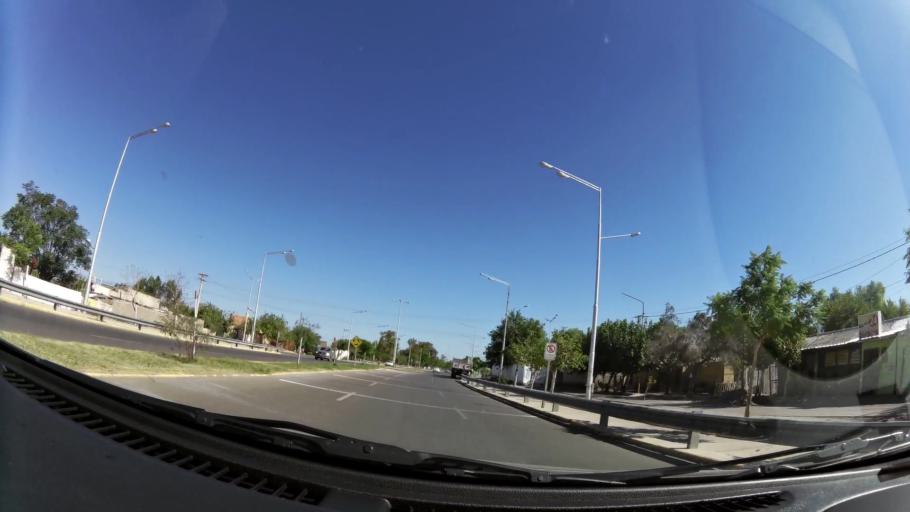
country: AR
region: San Juan
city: San Juan
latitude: -31.5473
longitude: -68.5366
